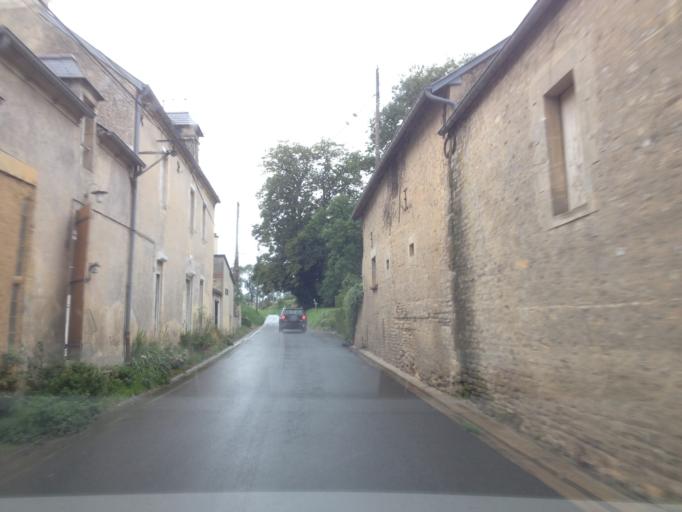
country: FR
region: Lower Normandy
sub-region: Departement du Calvados
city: Bayeux
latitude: 49.3020
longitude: -0.7087
